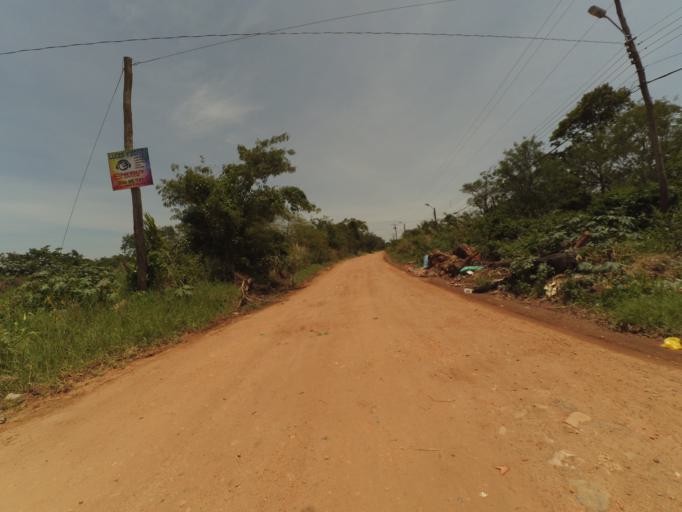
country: BO
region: Santa Cruz
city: Santa Cruz de la Sierra
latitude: -17.8357
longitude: -63.2488
